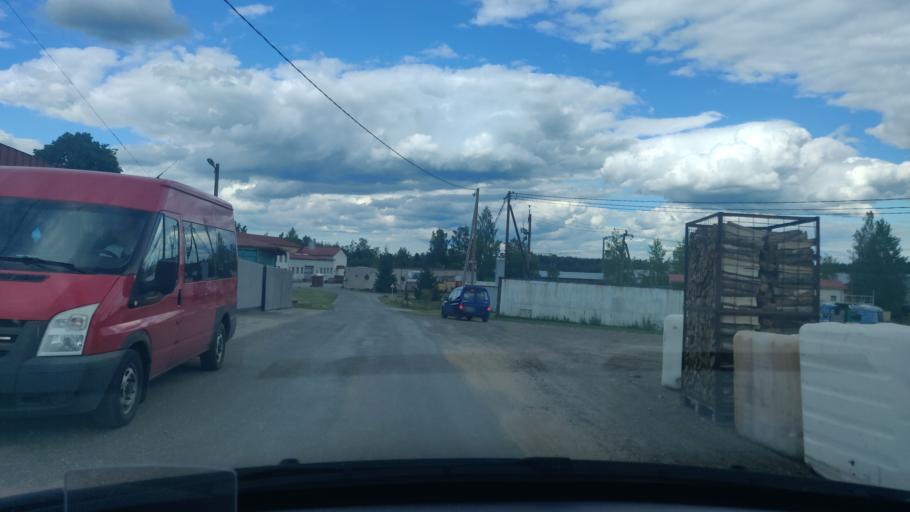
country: EE
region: Jogevamaa
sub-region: Mustvee linn
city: Mustvee
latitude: 58.9886
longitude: 26.8813
